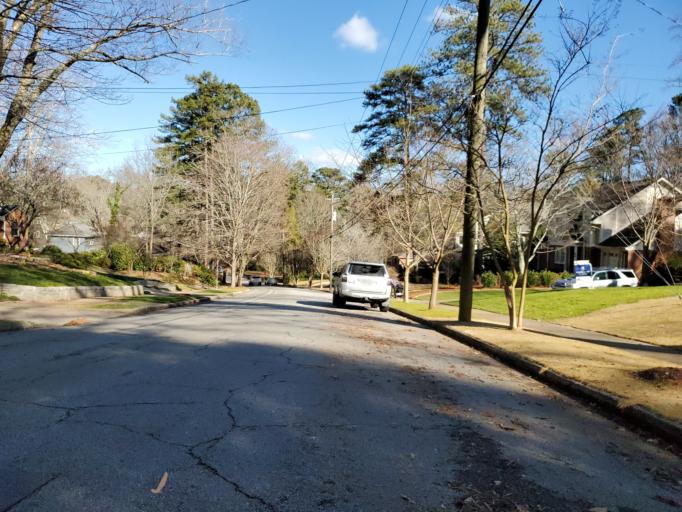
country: US
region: Georgia
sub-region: DeKalb County
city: Avondale Estates
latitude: 33.7649
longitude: -84.2654
